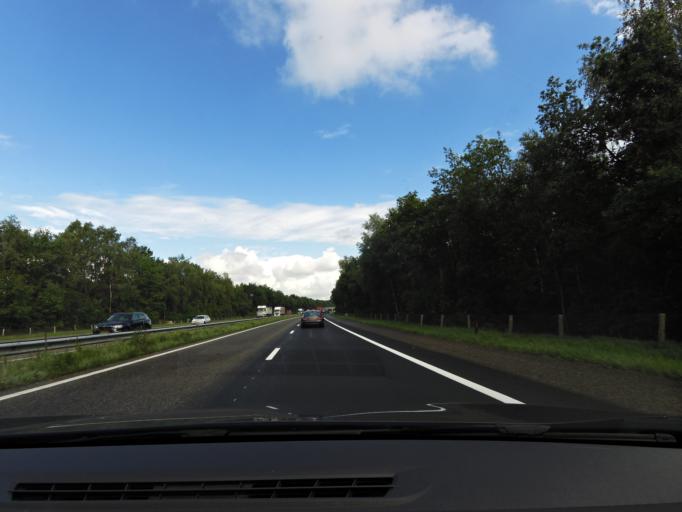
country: NL
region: North Brabant
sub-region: Gemeente Woensdrecht
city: Woensdrecht
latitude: 51.4640
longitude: 4.3114
